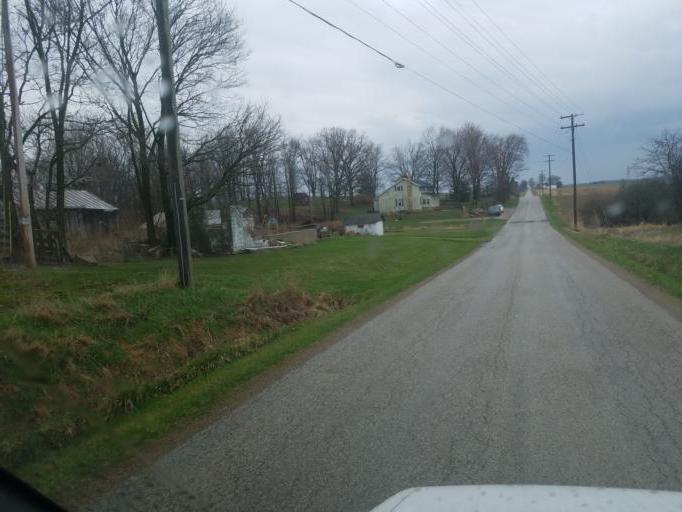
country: US
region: Ohio
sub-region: Crawford County
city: Galion
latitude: 40.6943
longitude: -82.8446
